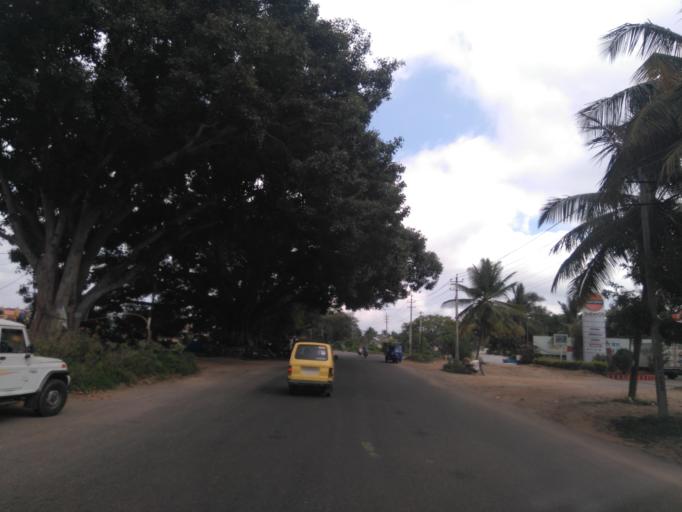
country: IN
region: Karnataka
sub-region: Mysore
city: Mysore
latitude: 12.2943
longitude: 76.7049
